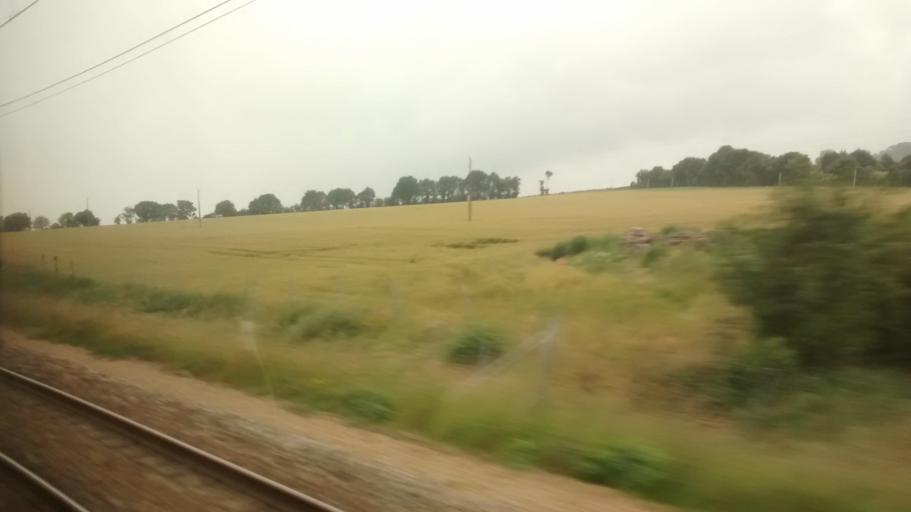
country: FR
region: Pays de la Loire
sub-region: Departement de la Sarthe
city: Vibraye
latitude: 48.0832
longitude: 0.8240
